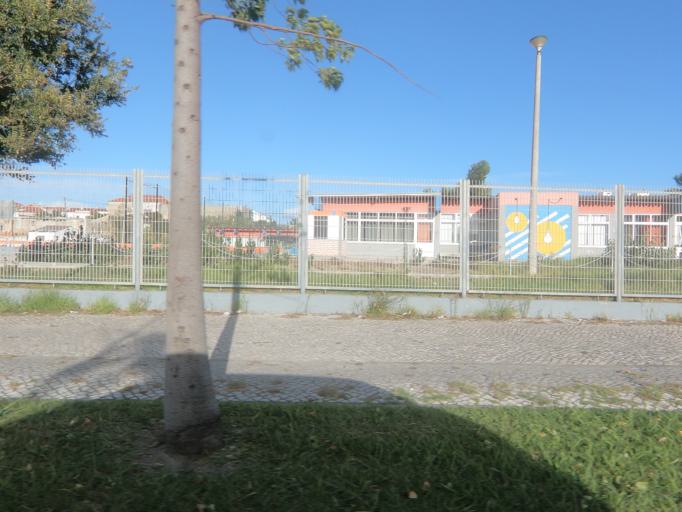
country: PT
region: Setubal
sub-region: Barreiro
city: Barreiro
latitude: 38.6634
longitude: -9.0551
